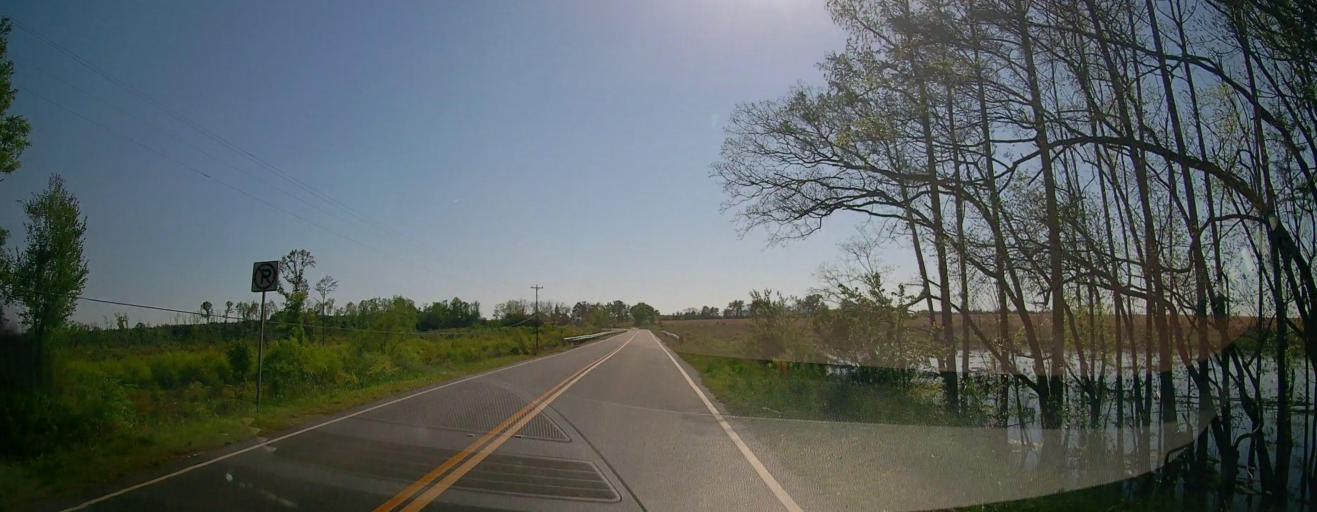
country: US
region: Georgia
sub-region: Wilcox County
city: Rochelle
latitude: 31.9119
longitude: -83.4755
